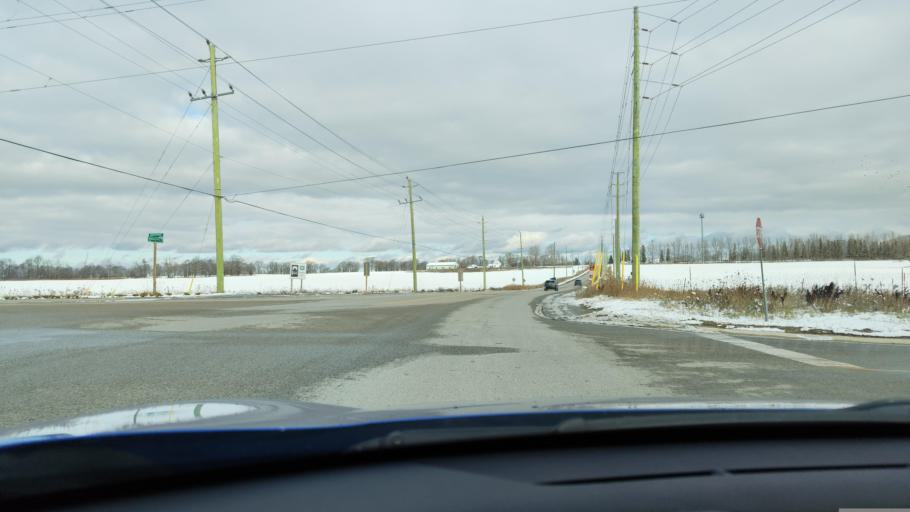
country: CA
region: Ontario
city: Barrie
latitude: 44.3914
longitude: -79.7544
